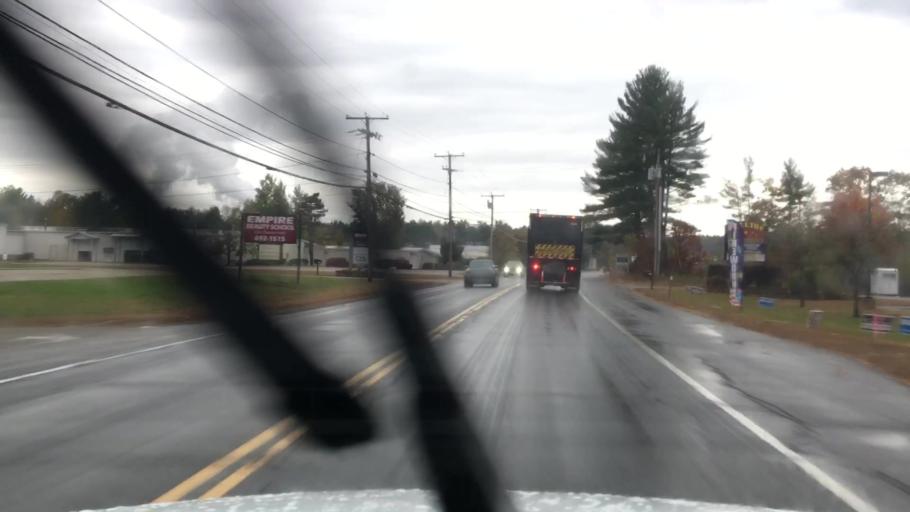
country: US
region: New Hampshire
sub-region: Strafford County
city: Somersworth
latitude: 43.2592
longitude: -70.9035
